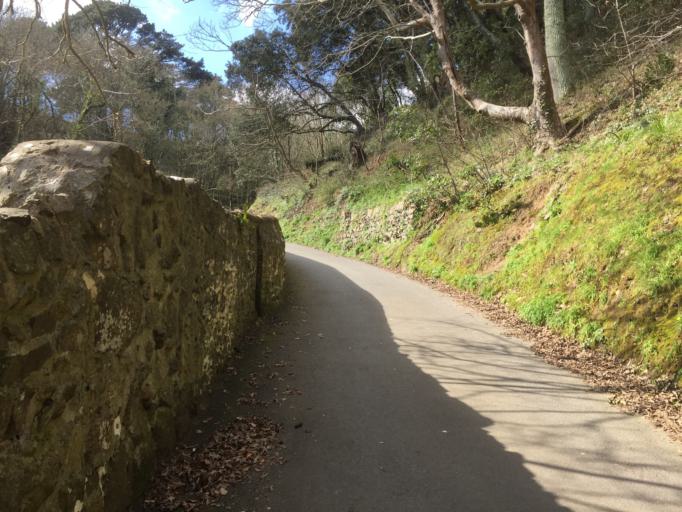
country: GG
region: St Peter Port
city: Saint Peter Port
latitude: 49.4276
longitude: -2.5501
